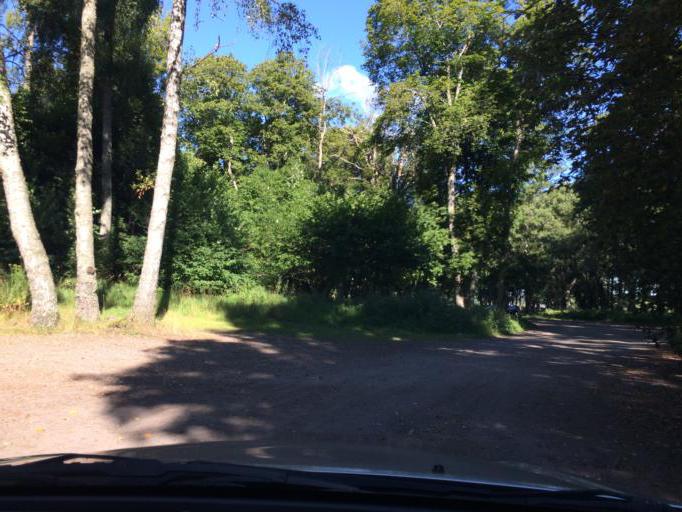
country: SE
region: Vaestmanland
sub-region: Vasteras
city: Vasteras
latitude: 59.5797
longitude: 16.6077
